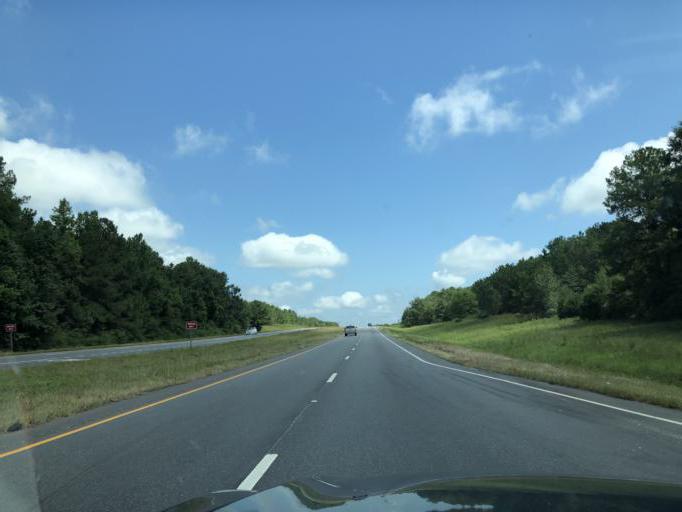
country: US
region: Alabama
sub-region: Henry County
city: Abbeville
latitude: 31.4922
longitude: -85.2958
